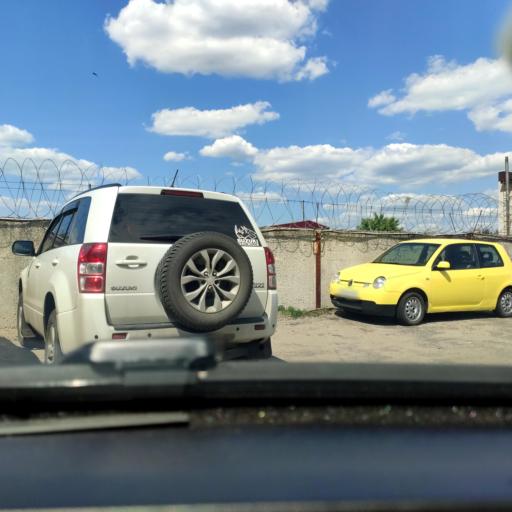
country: RU
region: Voronezj
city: Somovo
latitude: 51.7363
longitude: 39.3038
